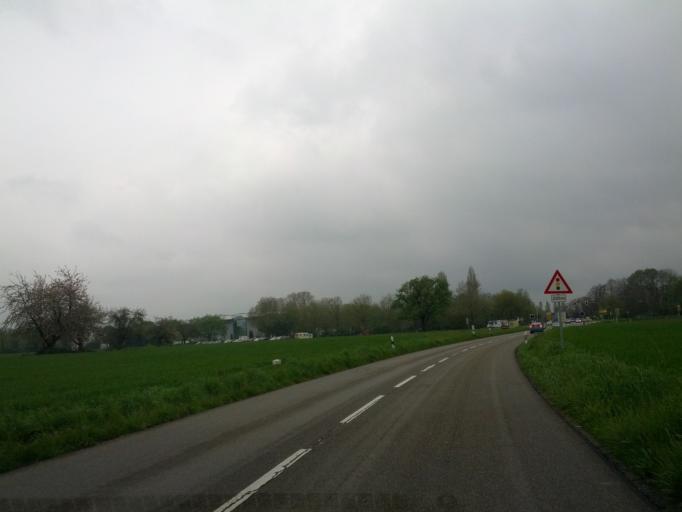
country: DE
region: Baden-Wuerttemberg
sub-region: Freiburg Region
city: Bad Krozingen
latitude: 47.8922
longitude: 7.7296
